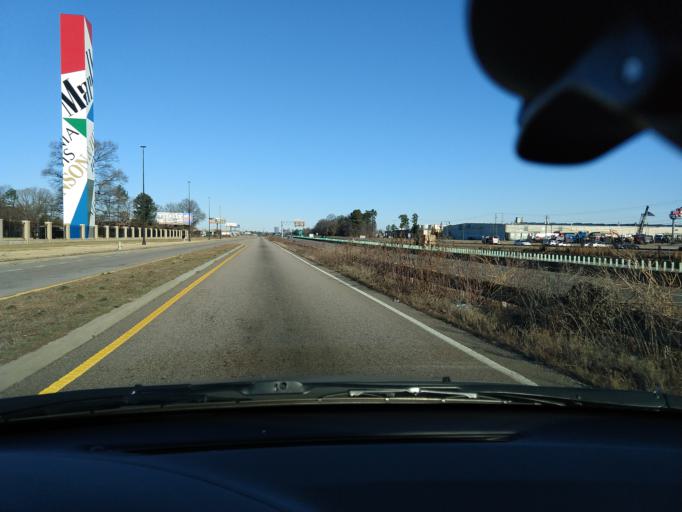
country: US
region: Virginia
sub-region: Chesterfield County
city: Bensley
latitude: 37.4737
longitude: -77.4296
